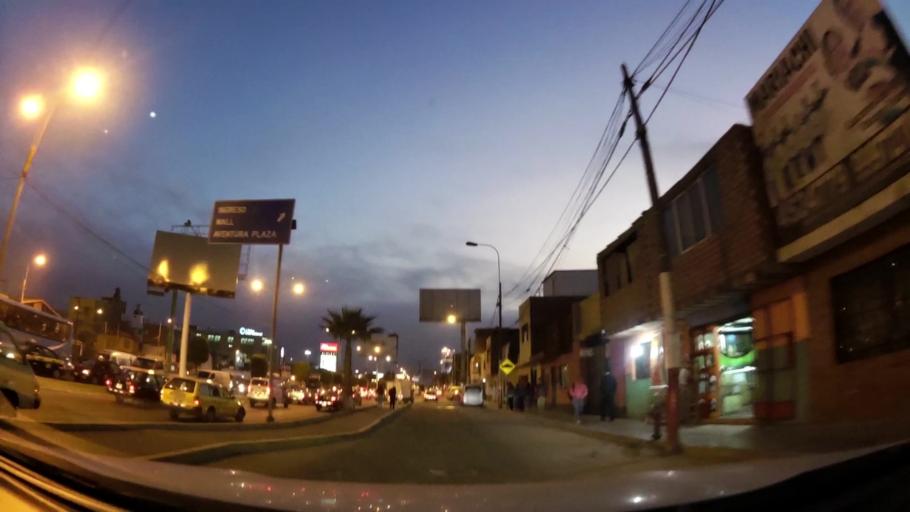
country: PE
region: Callao
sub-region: Callao
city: Callao
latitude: -12.0537
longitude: -77.0998
